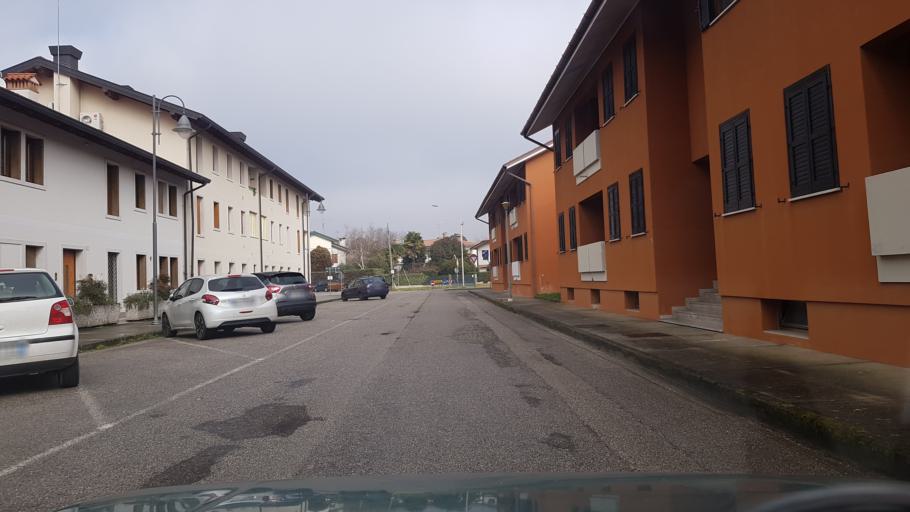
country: IT
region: Friuli Venezia Giulia
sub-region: Provincia di Udine
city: Palmanova
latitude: 45.9049
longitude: 13.3141
